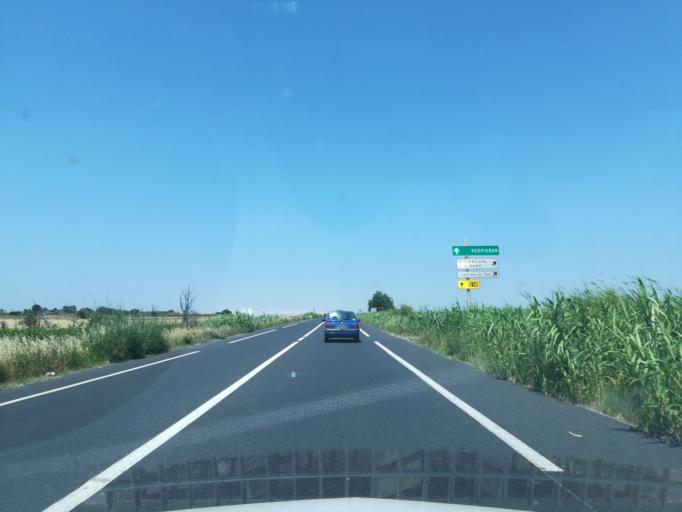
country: FR
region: Languedoc-Roussillon
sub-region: Departement des Pyrenees-Orientales
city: Pollestres
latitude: 42.6499
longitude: 2.8798
